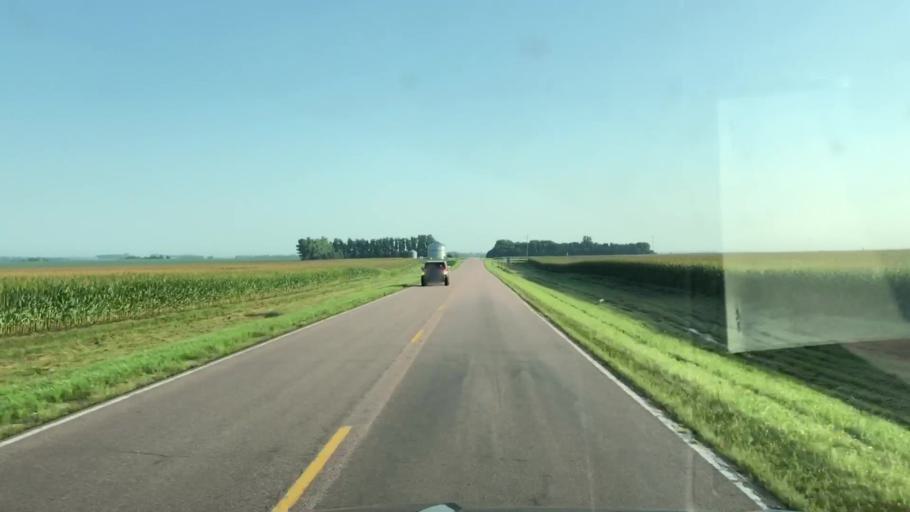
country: US
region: Iowa
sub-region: Lyon County
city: George
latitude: 43.3135
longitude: -95.9990
